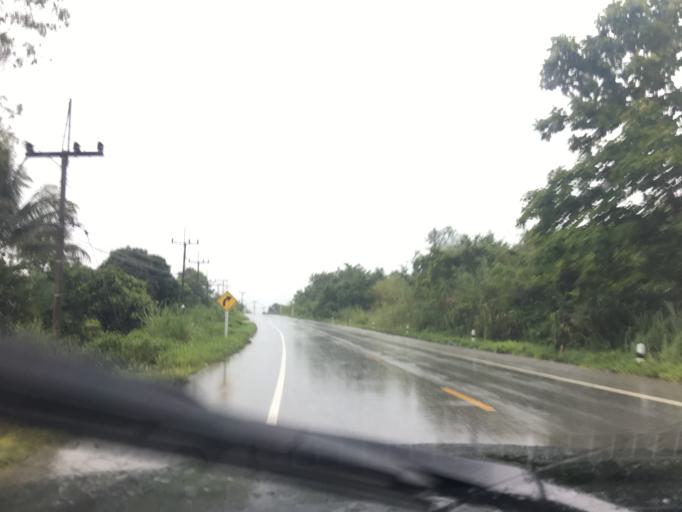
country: TH
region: Chiang Rai
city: Chiang Saen
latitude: 20.2635
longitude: 100.1892
